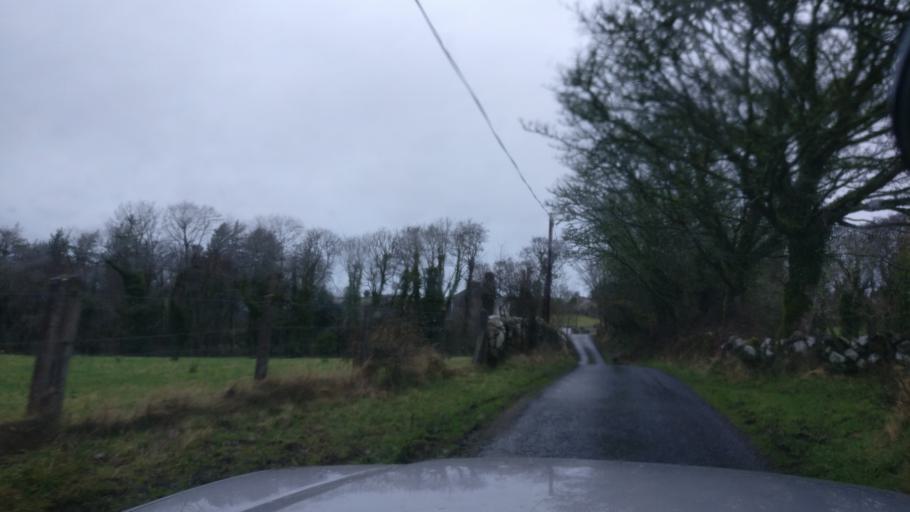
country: IE
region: Connaught
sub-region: County Galway
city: Loughrea
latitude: 53.1574
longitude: -8.6105
